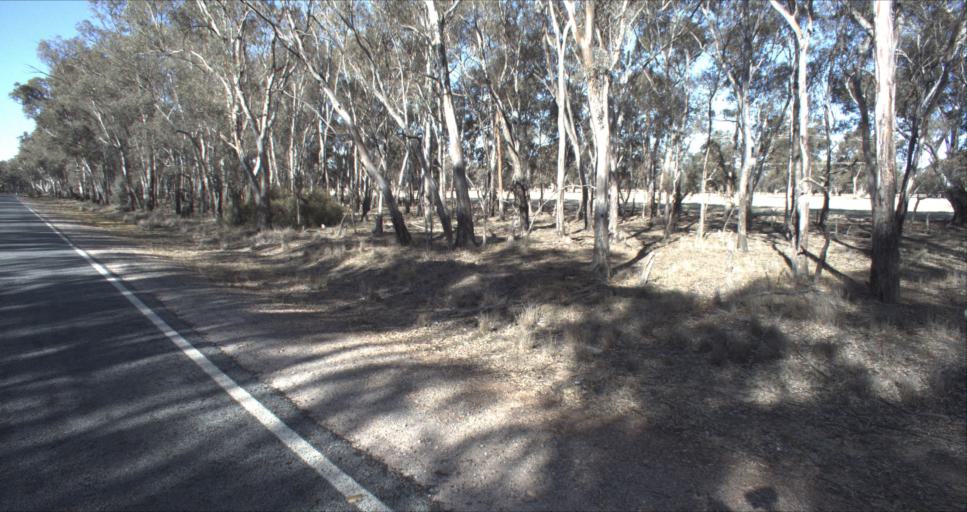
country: AU
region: New South Wales
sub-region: Leeton
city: Leeton
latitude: -34.6285
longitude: 146.3775
